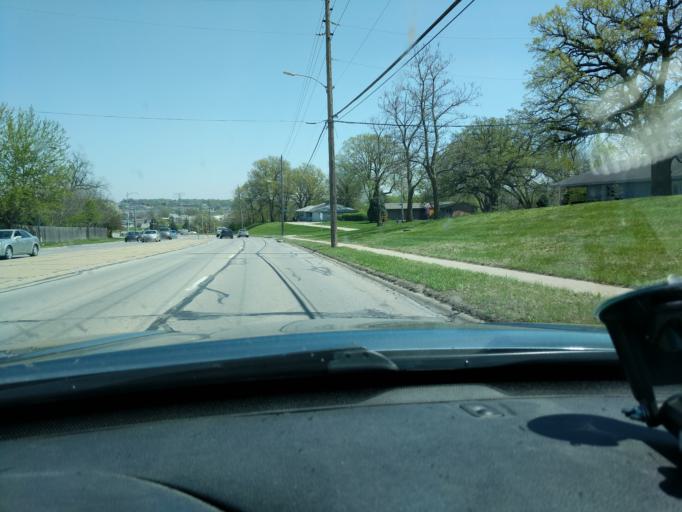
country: US
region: Nebraska
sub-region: Douglas County
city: Ralston
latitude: 41.2336
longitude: -96.0613
